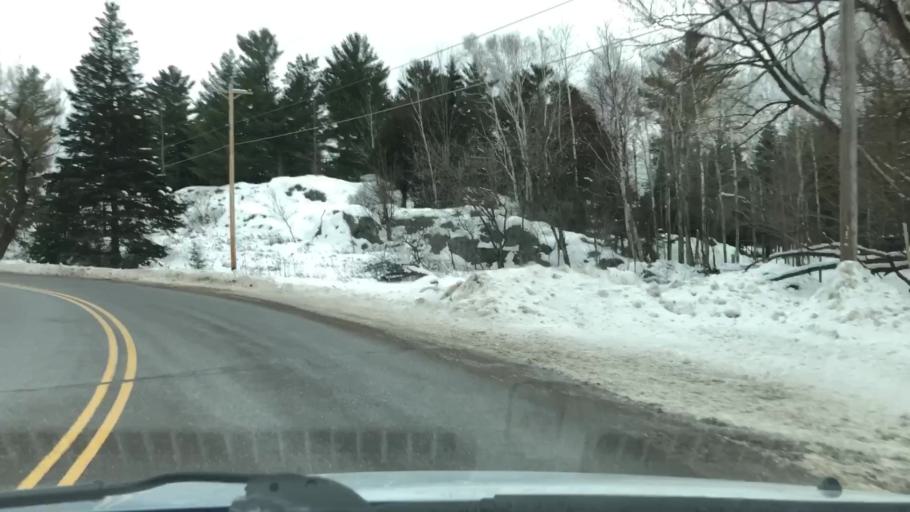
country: US
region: Minnesota
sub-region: Carlton County
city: Carlton
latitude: 46.6644
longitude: -92.3994
